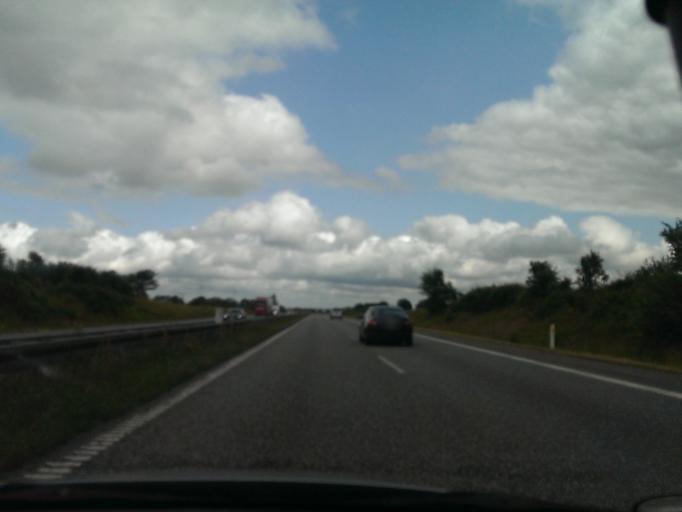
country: DK
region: North Denmark
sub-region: Mariagerfjord Kommune
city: Hobro
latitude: 56.6586
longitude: 9.7362
